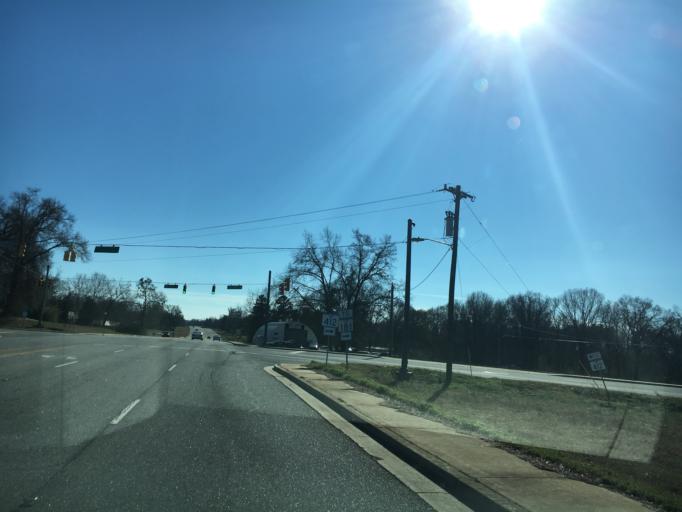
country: US
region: South Carolina
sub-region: Anderson County
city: Iva
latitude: 34.3770
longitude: -82.6948
